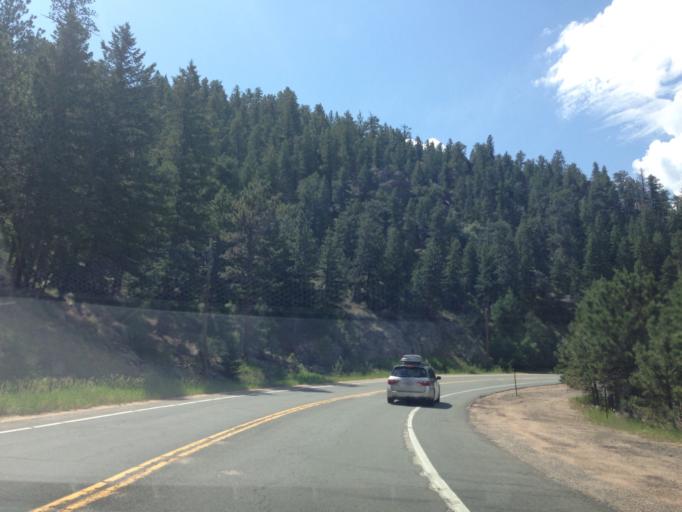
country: US
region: Colorado
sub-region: Larimer County
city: Estes Park
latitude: 40.4079
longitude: -105.4137
